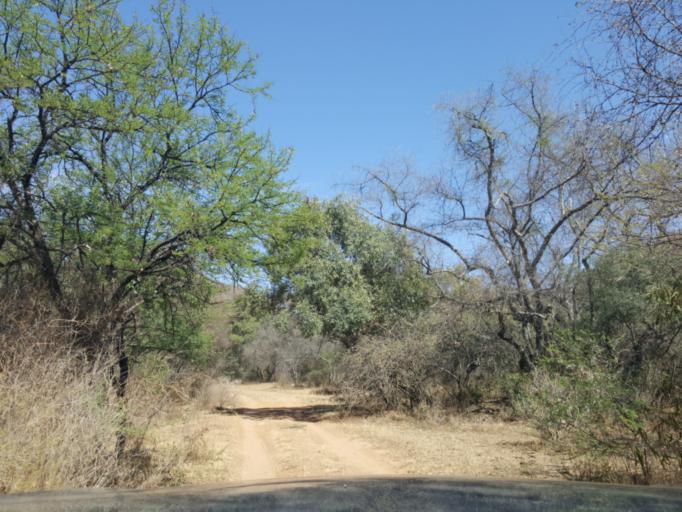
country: BW
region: South East
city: Lobatse
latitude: -25.1591
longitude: 25.6812
